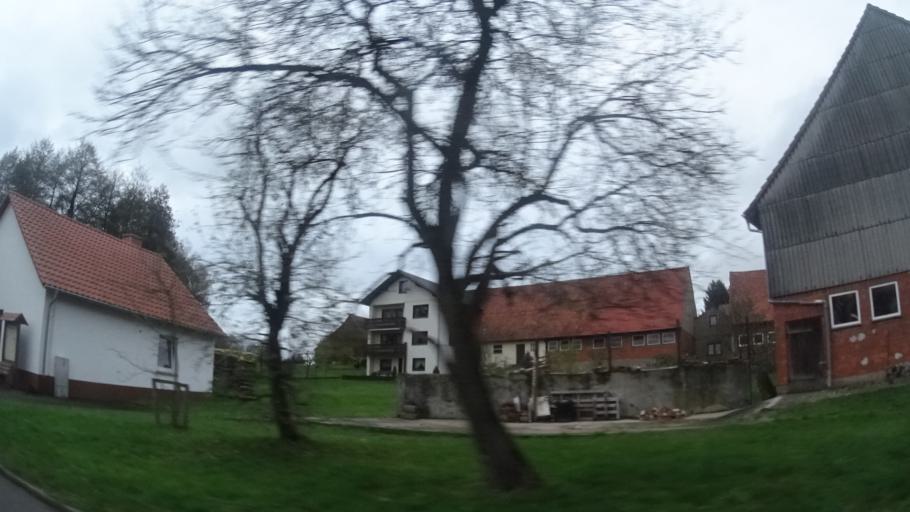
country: DE
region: Hesse
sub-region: Regierungsbezirk Giessen
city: Freiensteinau
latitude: 50.4151
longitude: 9.4192
